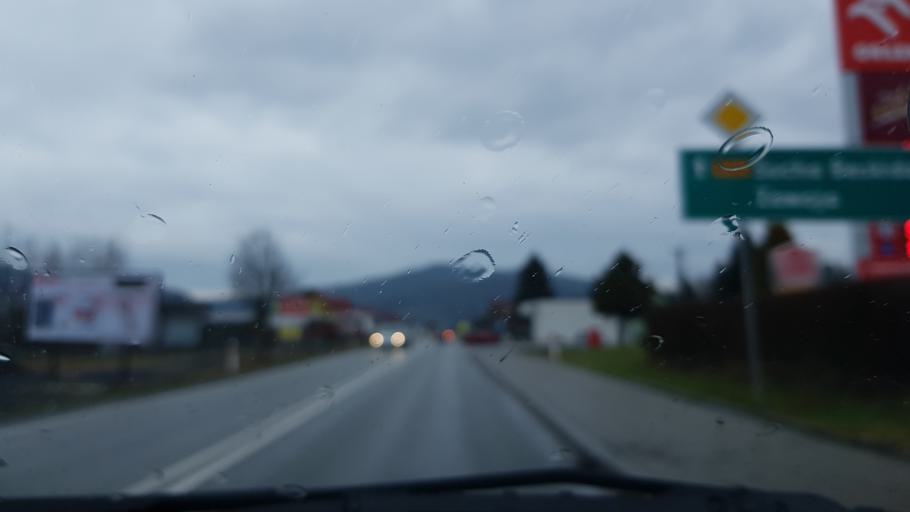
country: PL
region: Lesser Poland Voivodeship
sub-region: Powiat suski
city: Stryszawa
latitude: 49.7315
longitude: 19.5229
